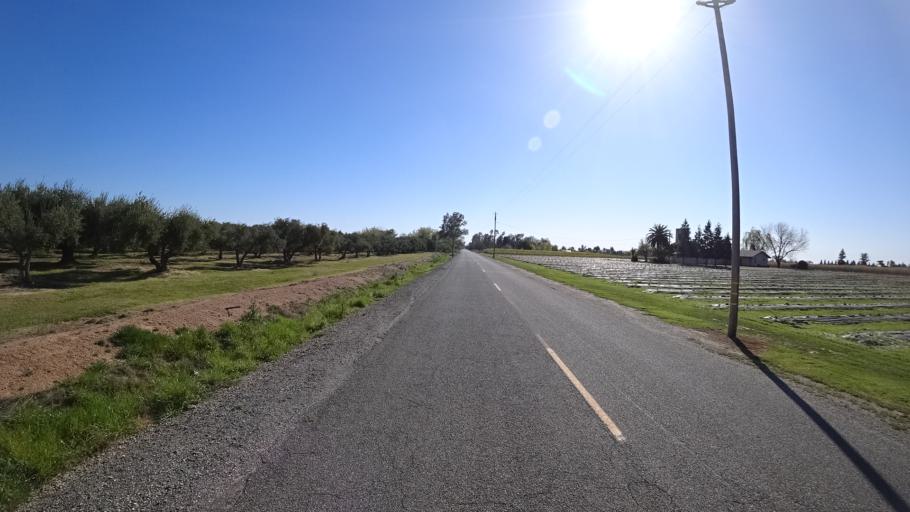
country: US
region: California
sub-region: Glenn County
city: Orland
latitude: 39.7442
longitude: -122.2335
